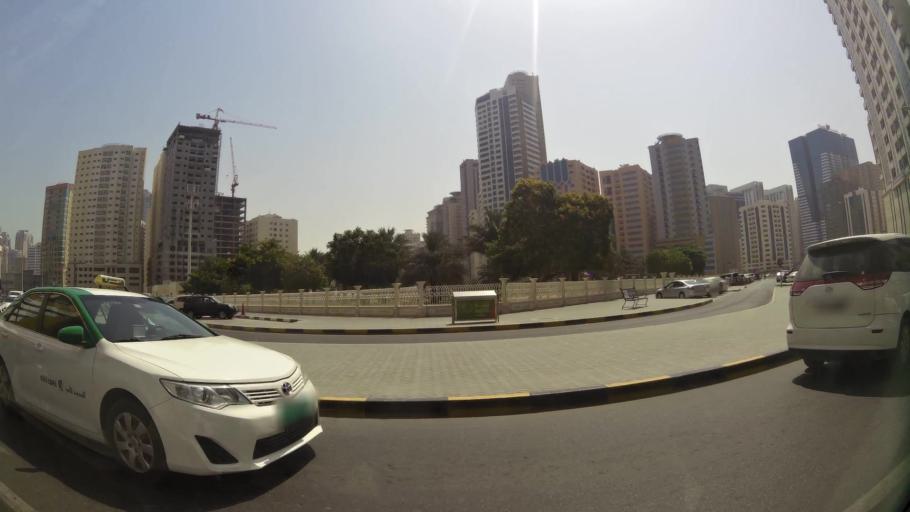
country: AE
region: Ash Shariqah
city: Sharjah
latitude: 25.3021
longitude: 55.3744
